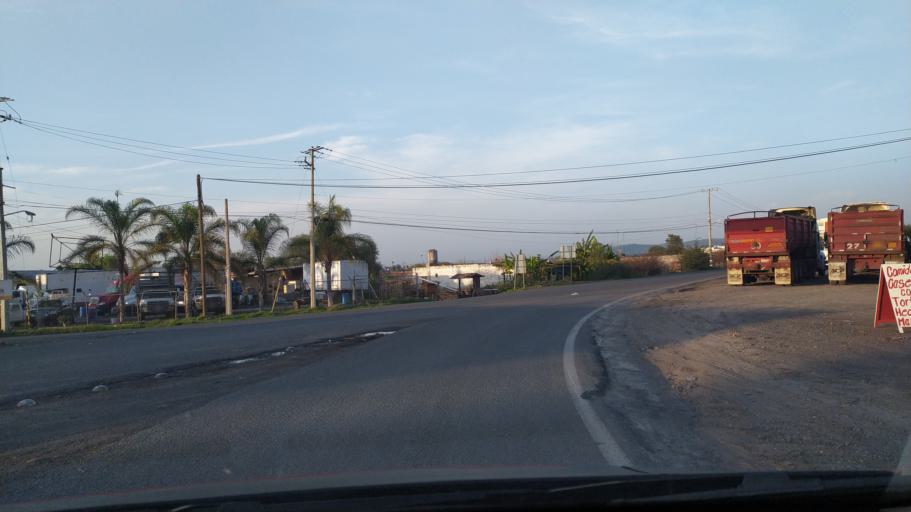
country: MX
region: Michoacan
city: Vistahermosa de Negrete
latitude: 20.2659
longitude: -102.4747
